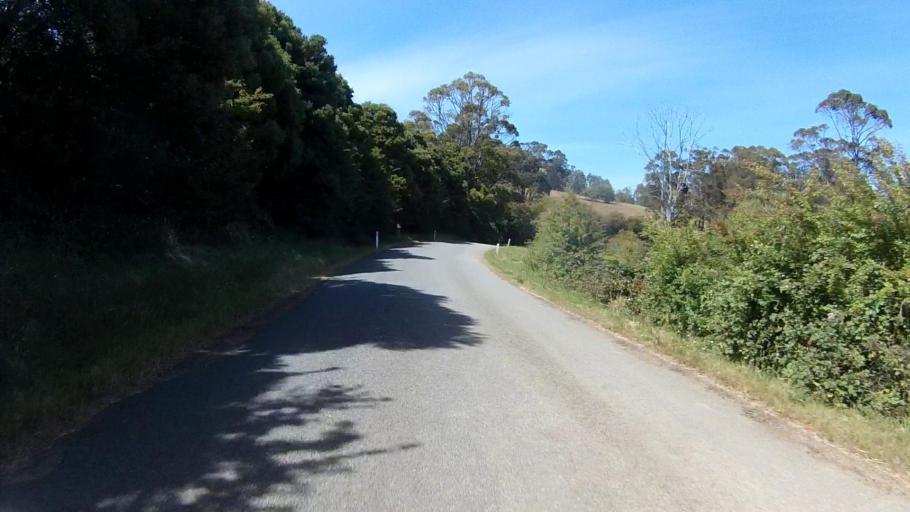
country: AU
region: Tasmania
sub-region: Sorell
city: Sorell
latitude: -42.7167
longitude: 147.7512
